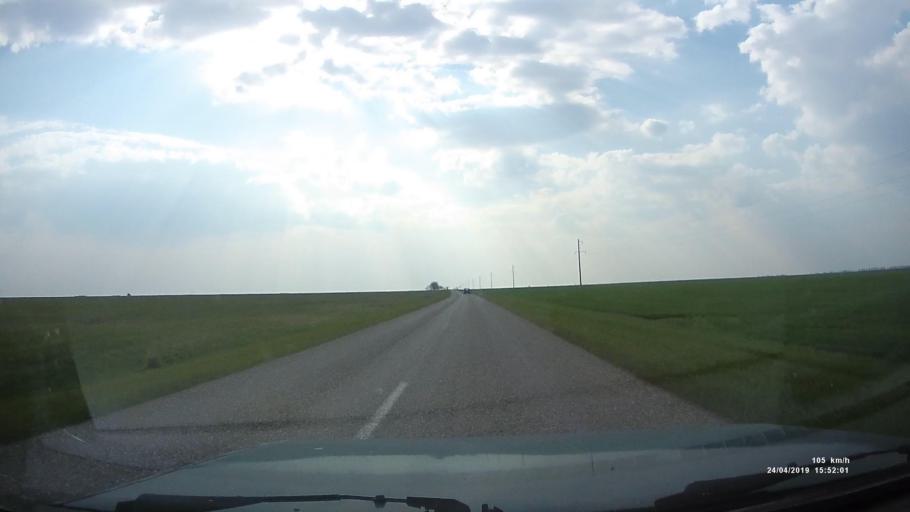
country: RU
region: Kalmykiya
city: Yashalta
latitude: 46.6045
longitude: 42.5976
